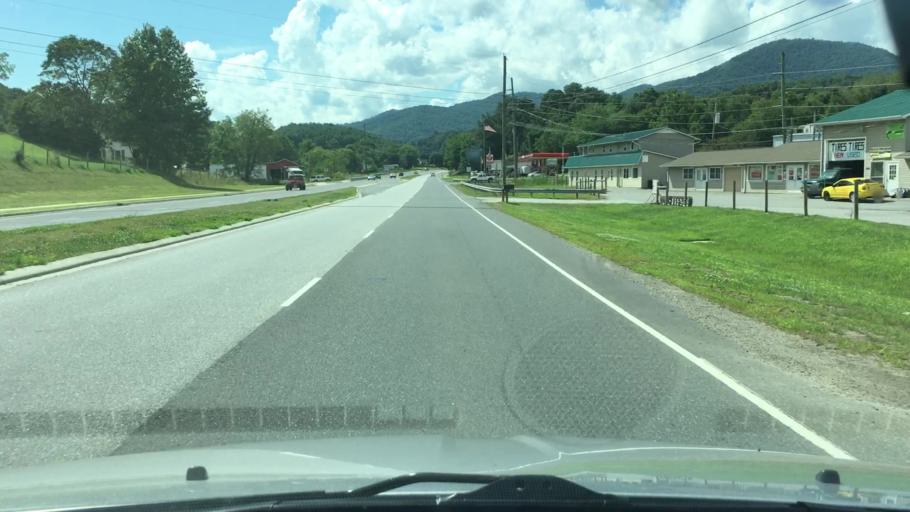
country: US
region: North Carolina
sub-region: Yancey County
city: Burnsville
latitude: 35.9145
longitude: -82.2637
